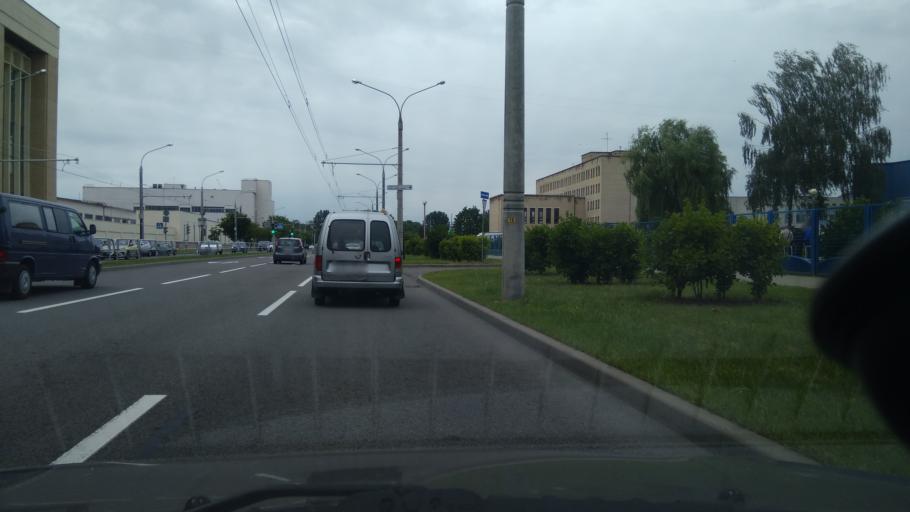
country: BY
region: Minsk
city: Minsk
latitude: 53.9233
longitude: 27.5198
